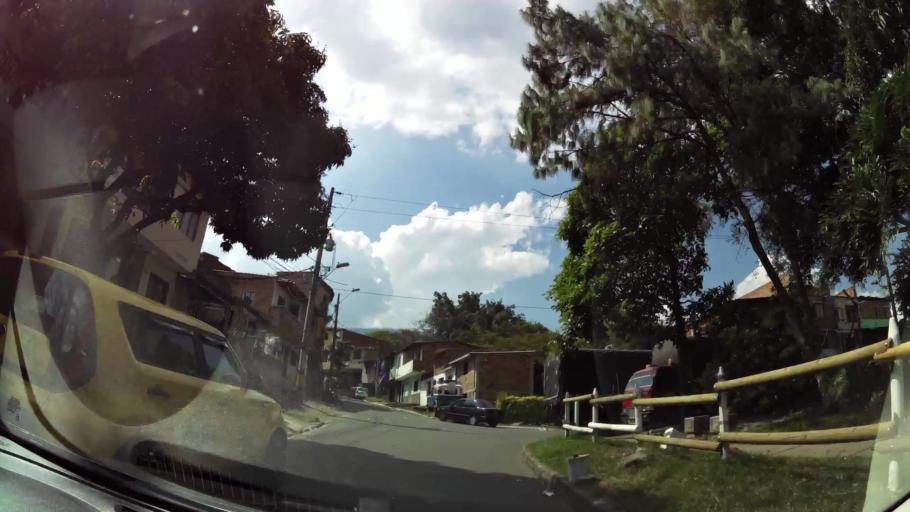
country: CO
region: Antioquia
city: Medellin
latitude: 6.2859
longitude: -75.5766
